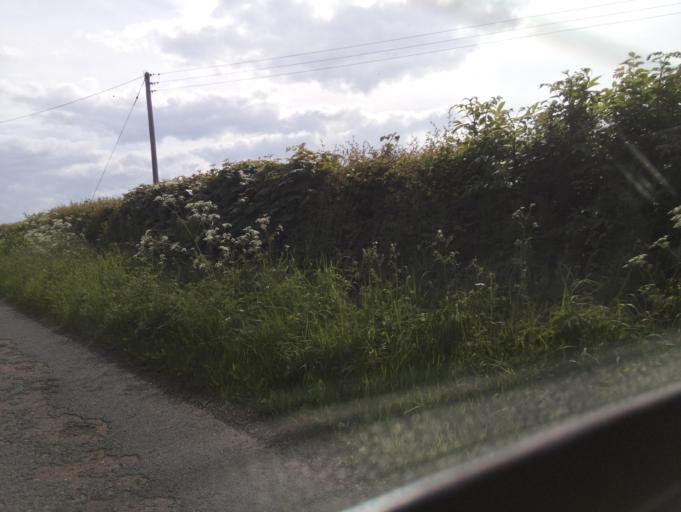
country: GB
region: England
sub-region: Northumberland
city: Ellingham
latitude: 55.4741
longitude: -1.7200
